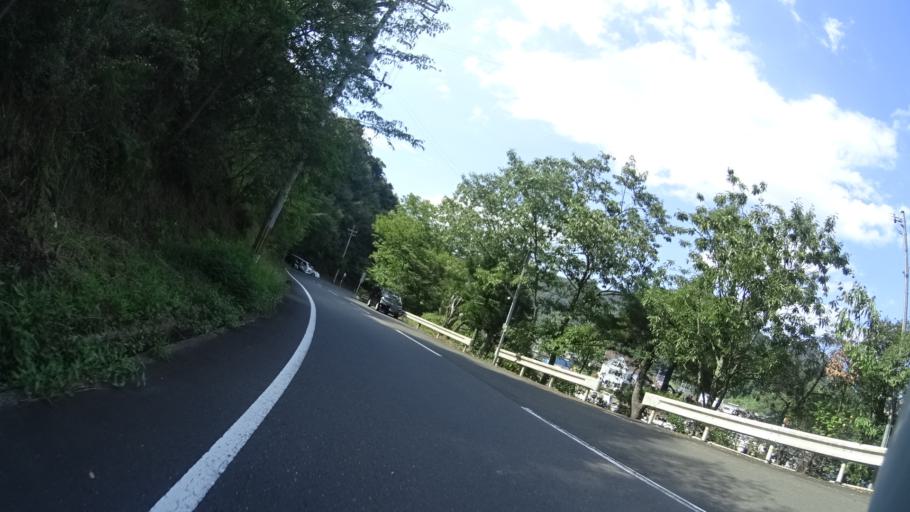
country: JP
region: Kyoto
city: Maizuru
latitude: 35.4778
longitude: 135.3169
